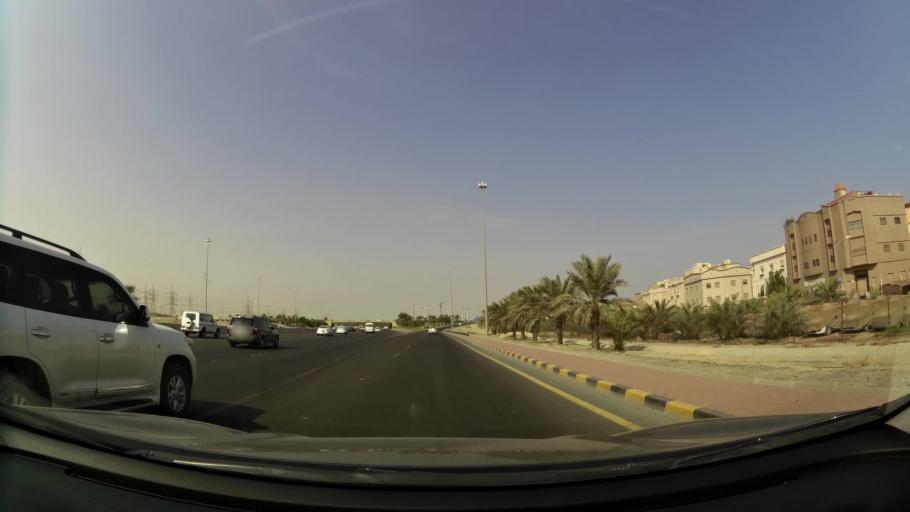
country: KW
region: Al Ahmadi
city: Ar Riqqah
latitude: 29.1269
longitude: 48.0926
